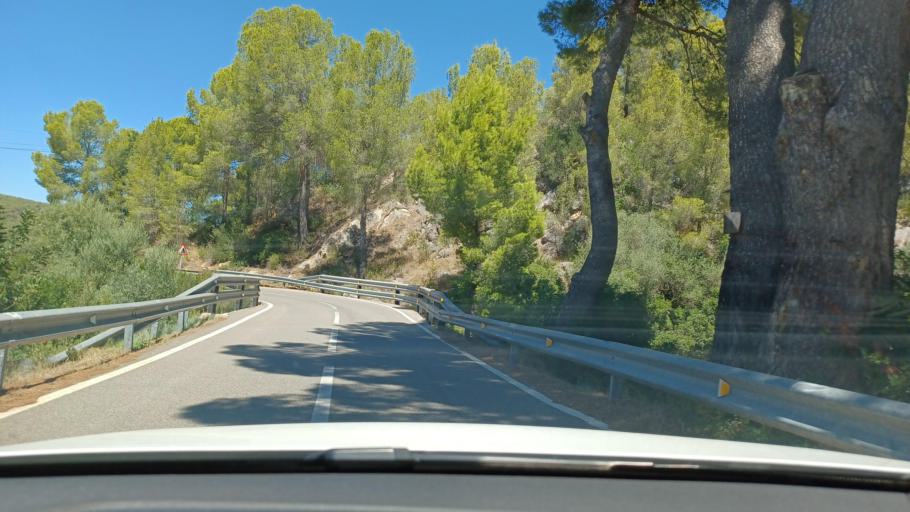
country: ES
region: Catalonia
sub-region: Provincia de Tarragona
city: Benifallet
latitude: 40.9541
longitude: 0.5044
